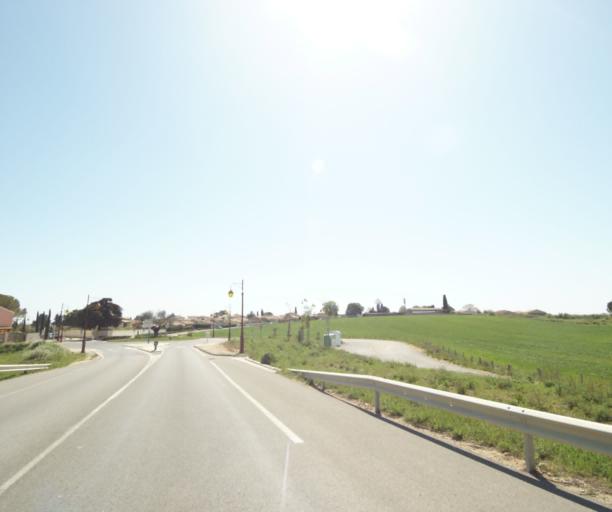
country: FR
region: Languedoc-Roussillon
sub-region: Departement de l'Herault
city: Baillargues
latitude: 43.6633
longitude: 4.0061
